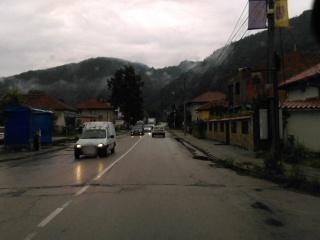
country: BG
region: Lovech
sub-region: Obshtina Troyan
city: Troyan
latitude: 42.8645
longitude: 24.7001
